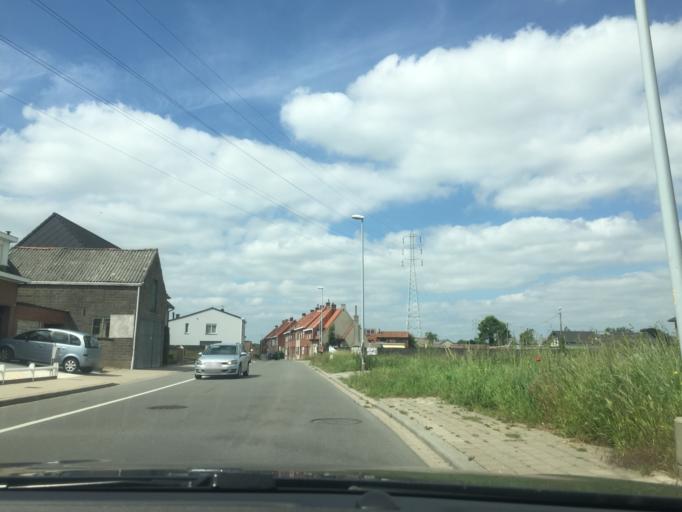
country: BE
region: Flanders
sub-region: Provincie West-Vlaanderen
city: Izegem
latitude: 50.9127
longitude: 3.2295
